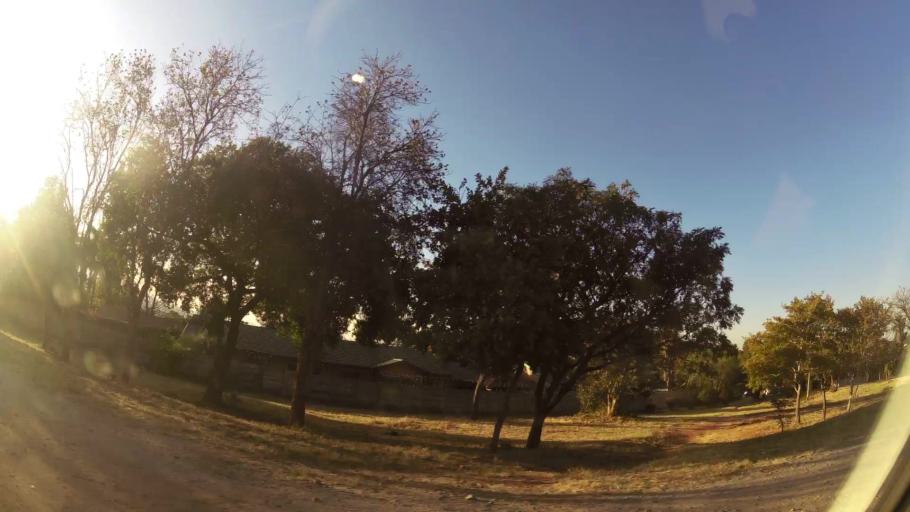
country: ZA
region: North-West
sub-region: Bojanala Platinum District Municipality
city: Rustenburg
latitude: -25.7022
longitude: 27.2255
